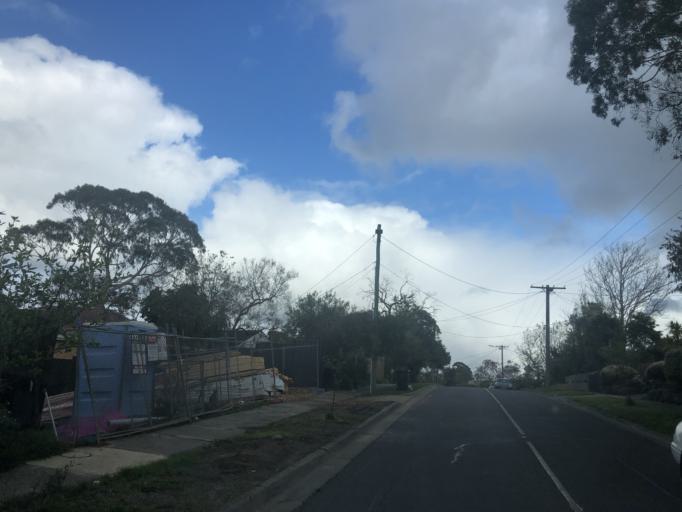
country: AU
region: Victoria
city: Burwood East
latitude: -37.8664
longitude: 145.1347
